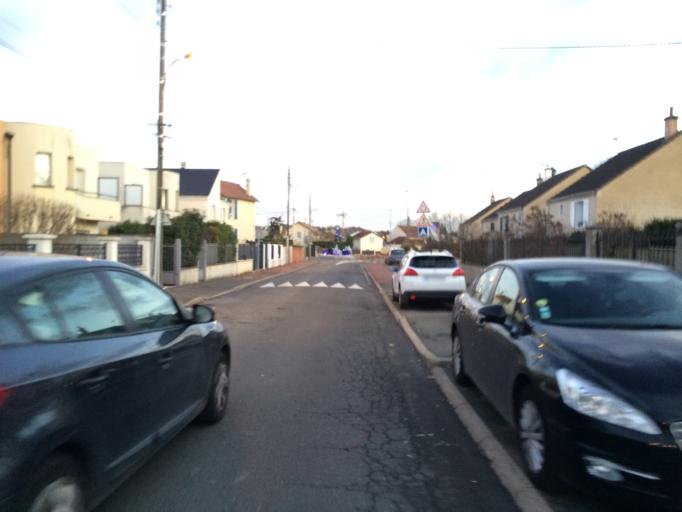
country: FR
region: Ile-de-France
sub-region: Departement de l'Essonne
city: Longjumeau
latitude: 48.6969
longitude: 2.3055
